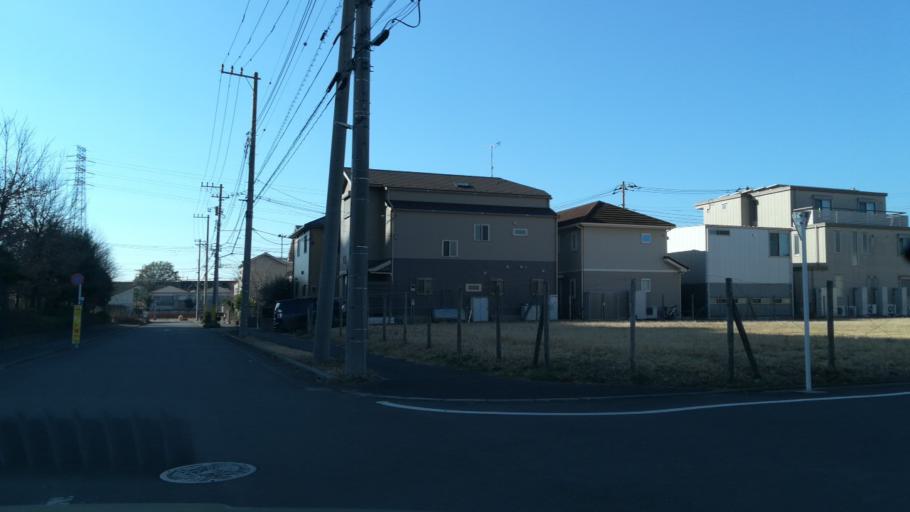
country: JP
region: Tokyo
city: Hino
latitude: 35.6818
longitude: 139.4085
